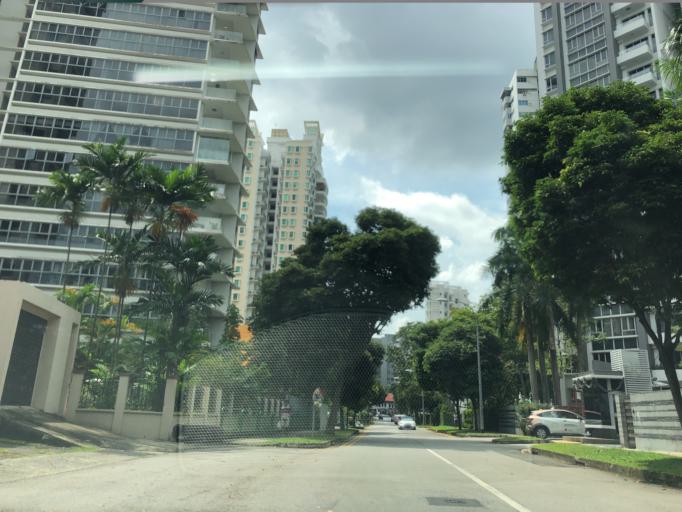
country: SG
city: Singapore
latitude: 1.3282
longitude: 103.8500
